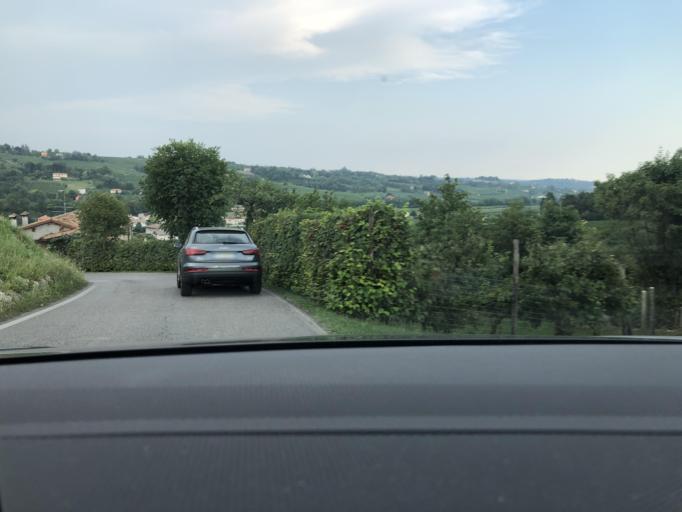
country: IT
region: Veneto
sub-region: Provincia di Treviso
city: San Pietro di Feletto
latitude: 45.9266
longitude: 12.2522
